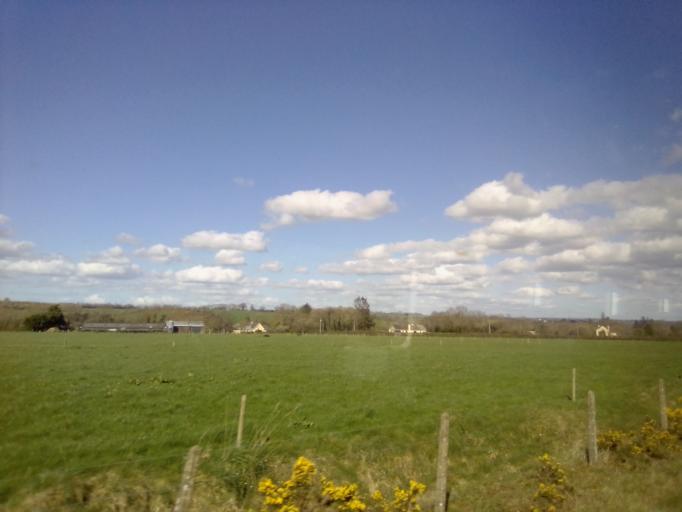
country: IE
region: Munster
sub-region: County Cork
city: Kanturk
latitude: 52.1185
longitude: -8.7973
